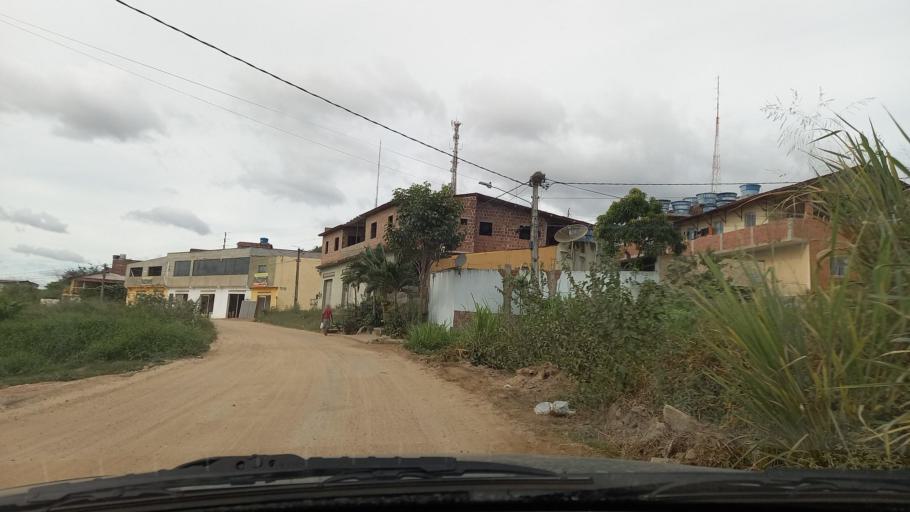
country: BR
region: Pernambuco
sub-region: Gravata
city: Gravata
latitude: -8.2125
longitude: -35.5773
